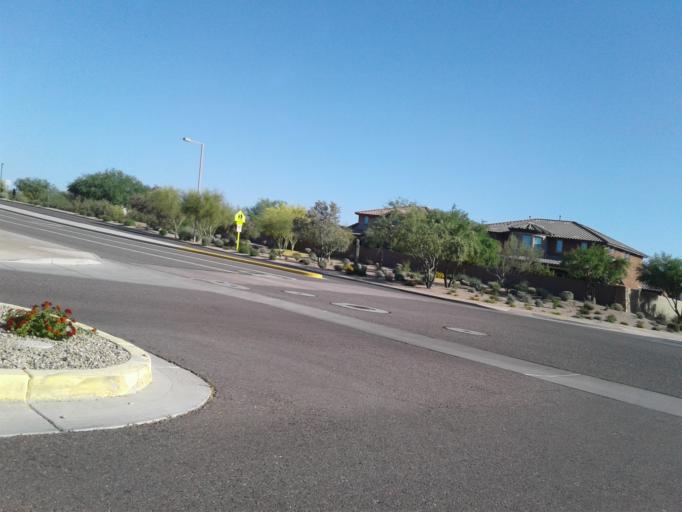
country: US
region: Arizona
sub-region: Maricopa County
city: Paradise Valley
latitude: 33.6798
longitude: -112.0030
